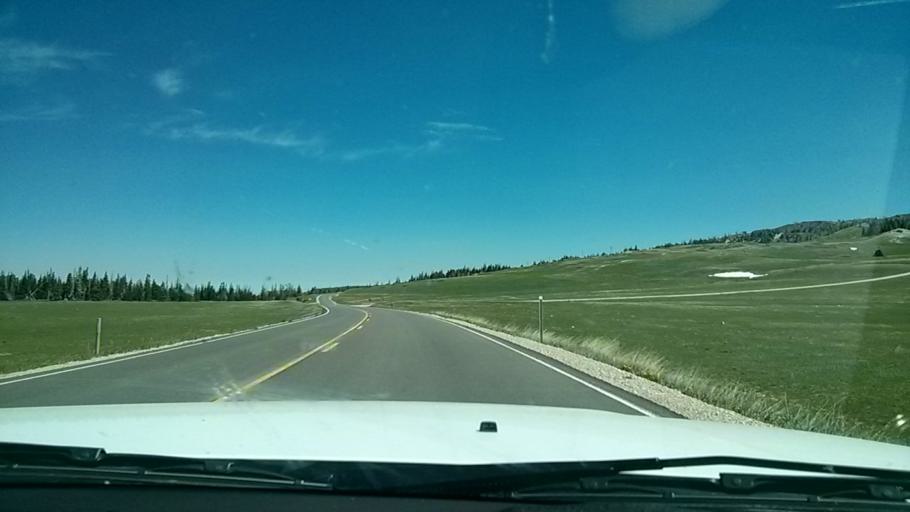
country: US
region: Utah
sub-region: Iron County
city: Parowan
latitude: 37.6666
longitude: -112.8380
